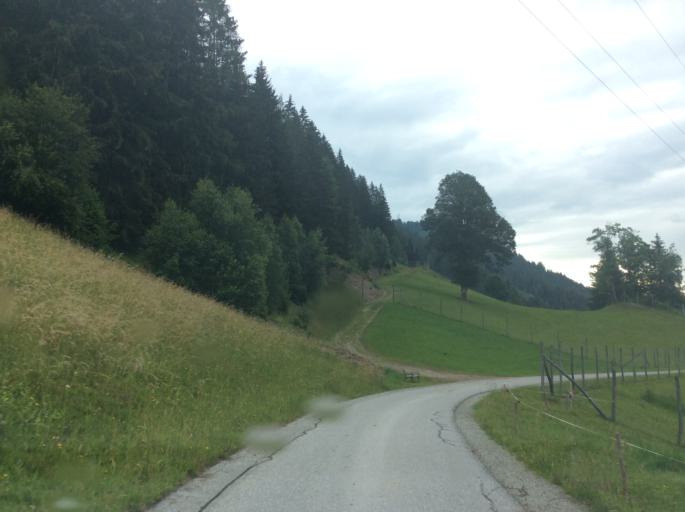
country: AT
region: Styria
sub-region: Politischer Bezirk Liezen
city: Schladming
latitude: 47.3906
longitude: 13.6322
